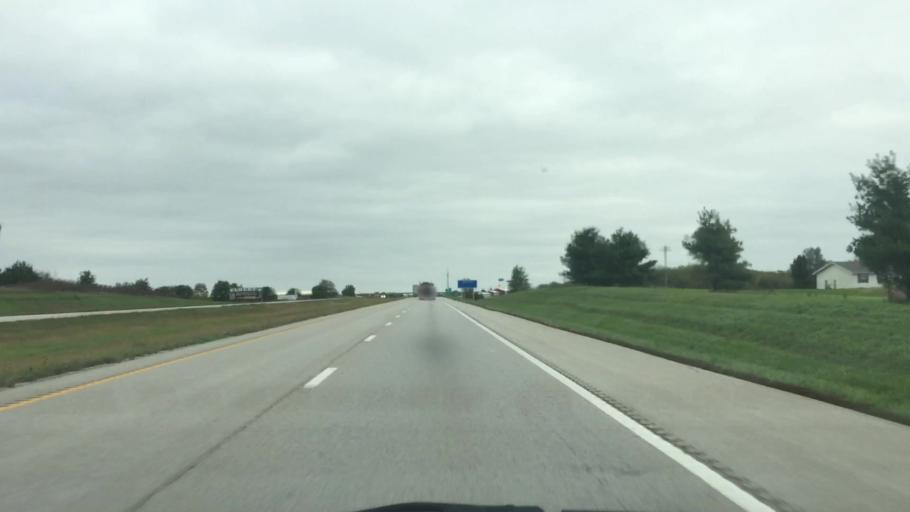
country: US
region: Missouri
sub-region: Clinton County
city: Cameron
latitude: 39.8447
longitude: -94.1805
